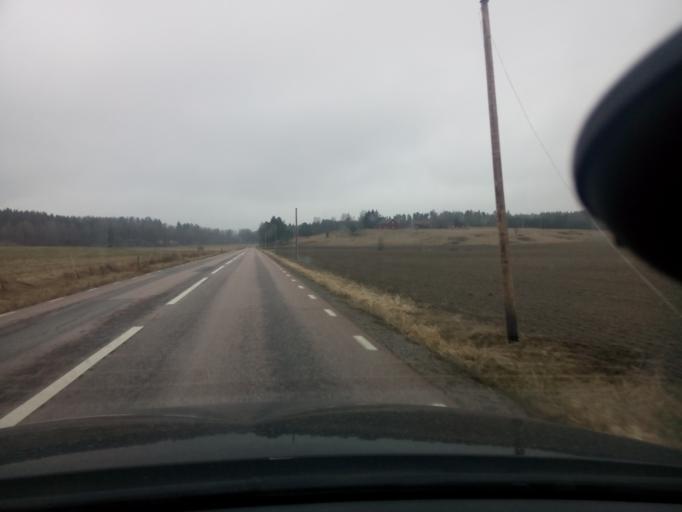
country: SE
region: Soedermanland
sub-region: Gnesta Kommun
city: Gnesta
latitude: 59.0204
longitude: 17.1693
